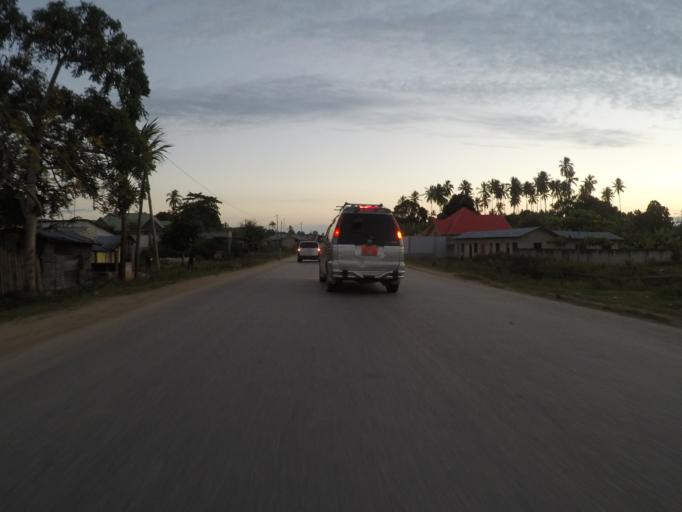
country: TZ
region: Zanzibar Central/South
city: Koani
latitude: -6.0331
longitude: 39.2359
